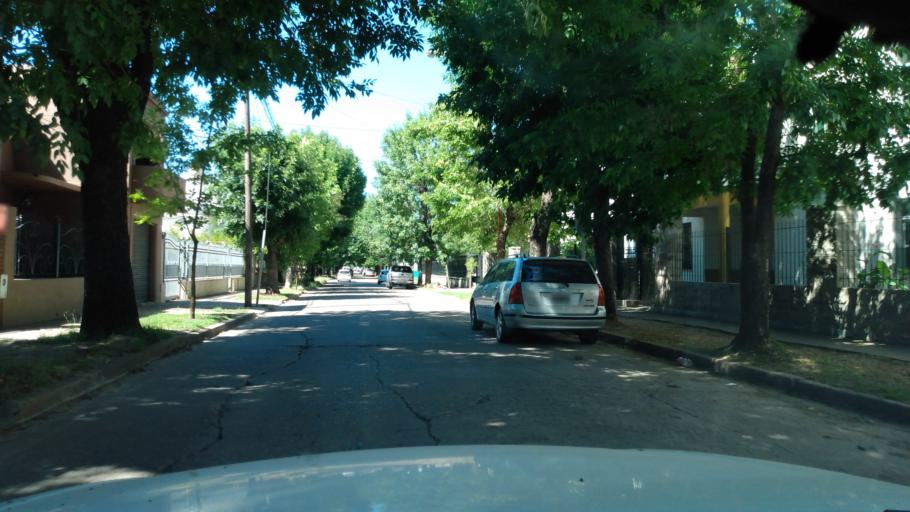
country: AR
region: Buenos Aires
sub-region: Partido de Lujan
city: Lujan
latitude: -34.5666
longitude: -59.1090
